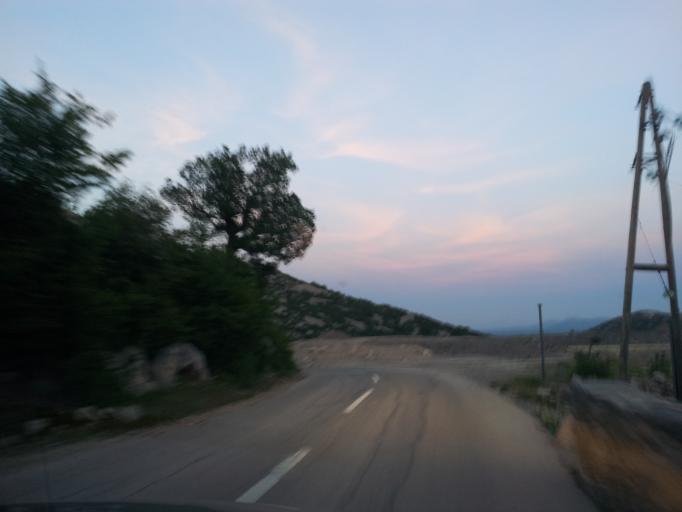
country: HR
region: Zadarska
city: Obrovac
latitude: 44.2515
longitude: 15.6484
